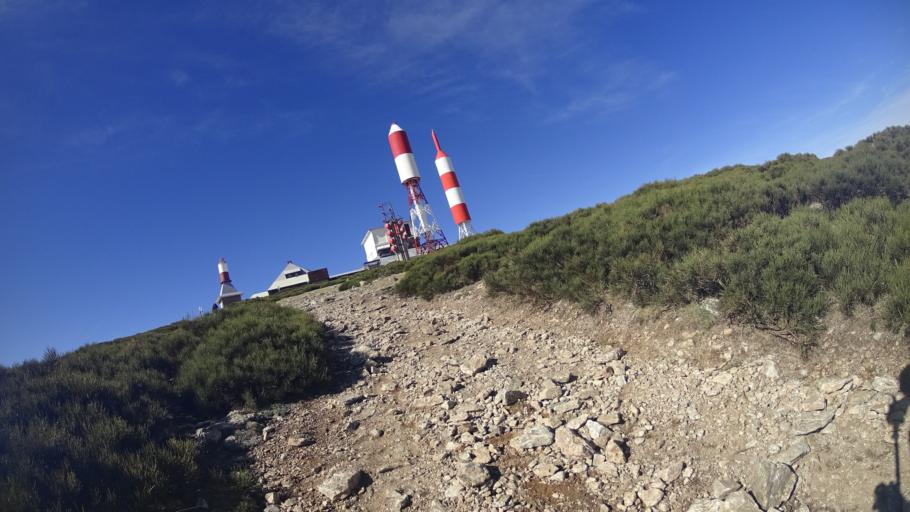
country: ES
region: Madrid
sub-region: Provincia de Madrid
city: Navacerrada
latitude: 40.7843
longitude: -3.9781
